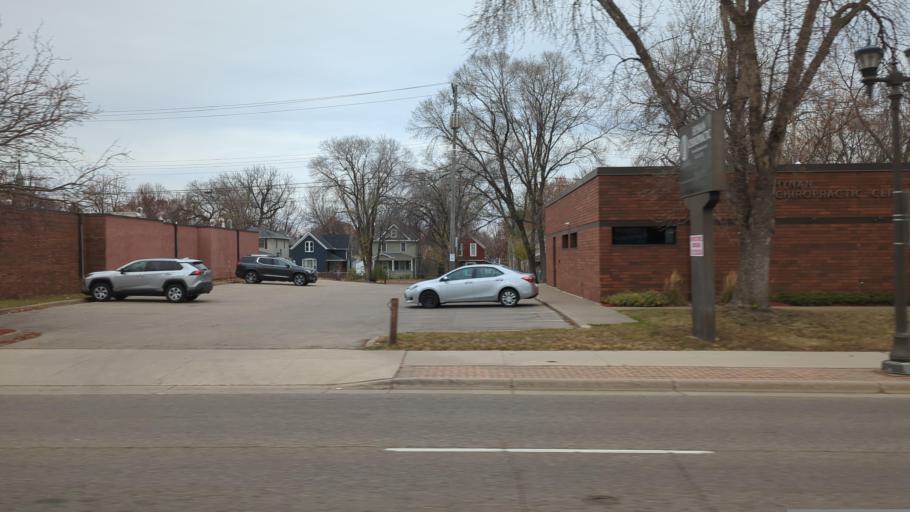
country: US
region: Minnesota
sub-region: Ramsey County
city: Saint Paul
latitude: 44.9559
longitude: -93.1204
